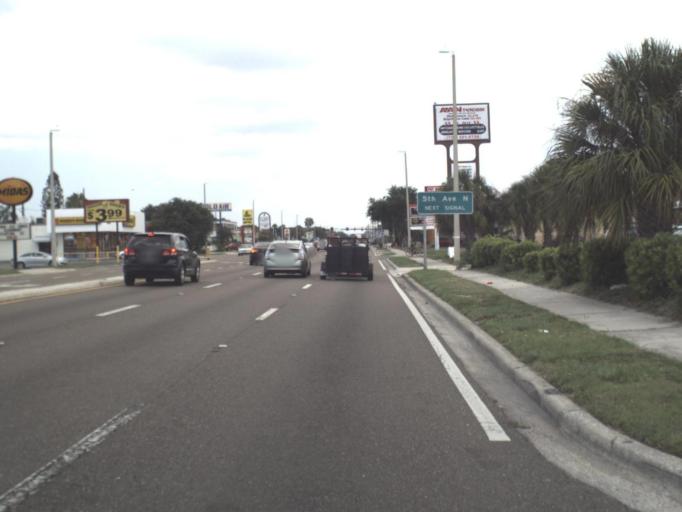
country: US
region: Florida
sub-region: Pinellas County
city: Saint Petersburg
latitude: 27.7738
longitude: -82.6793
